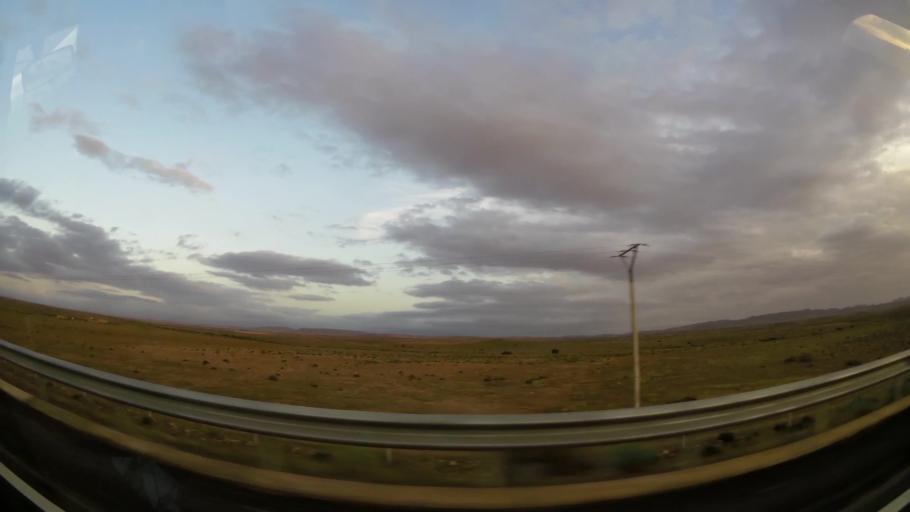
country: MA
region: Oriental
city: Taourirt
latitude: 34.5481
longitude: -2.8932
